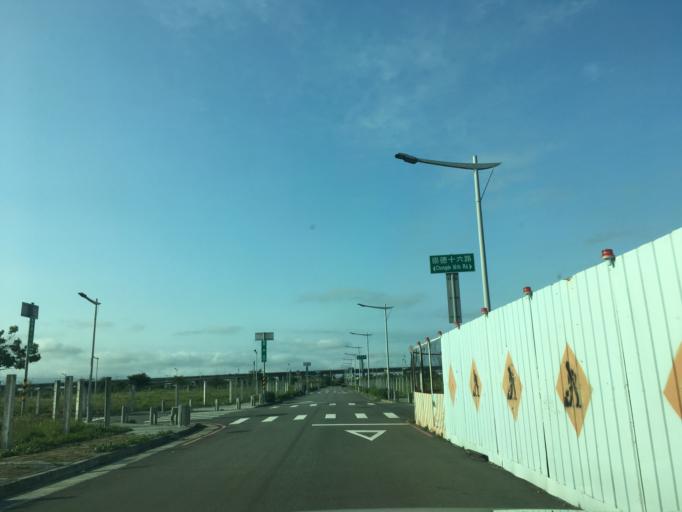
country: TW
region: Taiwan
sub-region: Taichung City
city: Taichung
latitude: 24.1950
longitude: 120.6924
